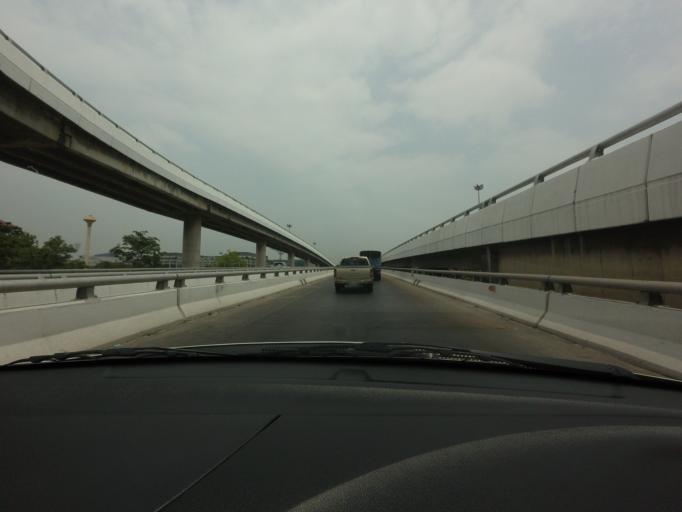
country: TH
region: Bangkok
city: Thawi Watthana
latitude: 13.7862
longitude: 100.3278
